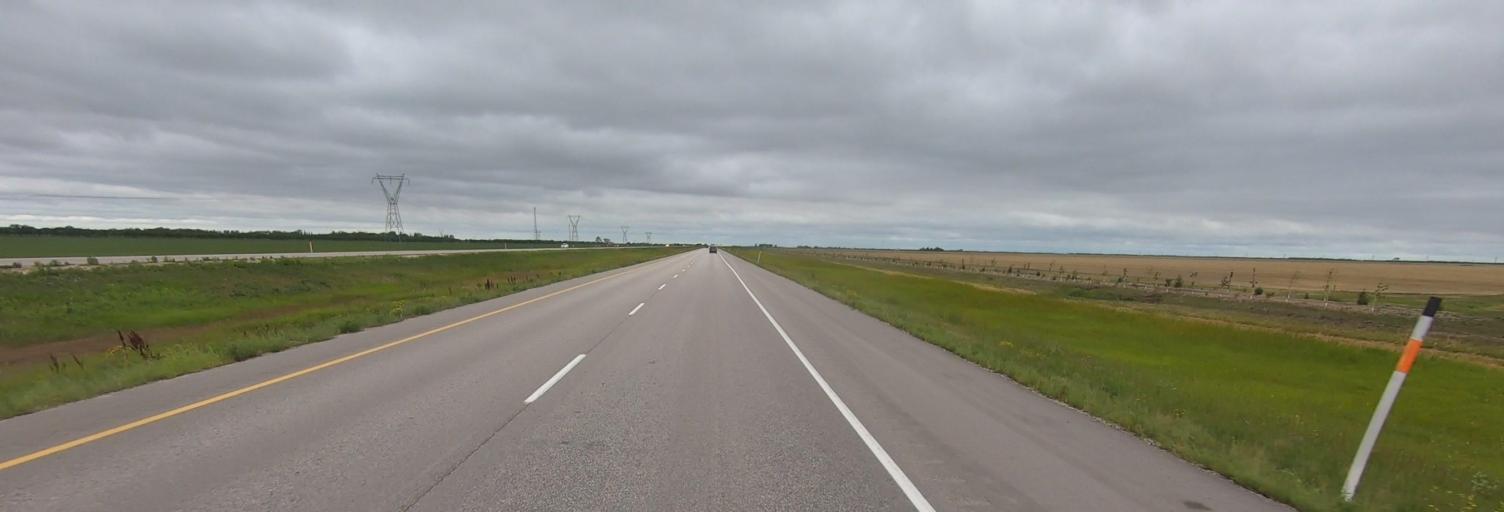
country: CA
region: Manitoba
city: Headingley
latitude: 49.8871
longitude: -97.6189
